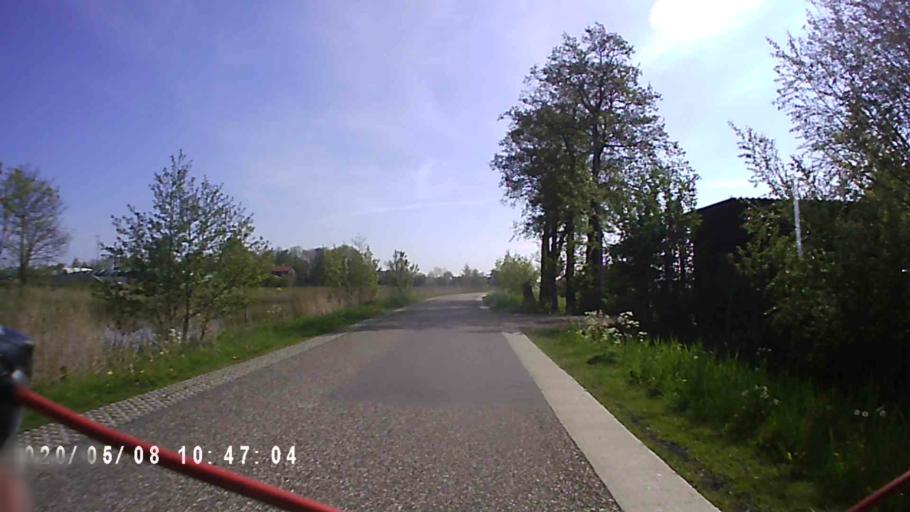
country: NL
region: Groningen
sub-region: Gemeente Winsum
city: Winsum
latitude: 53.3340
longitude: 6.5448
